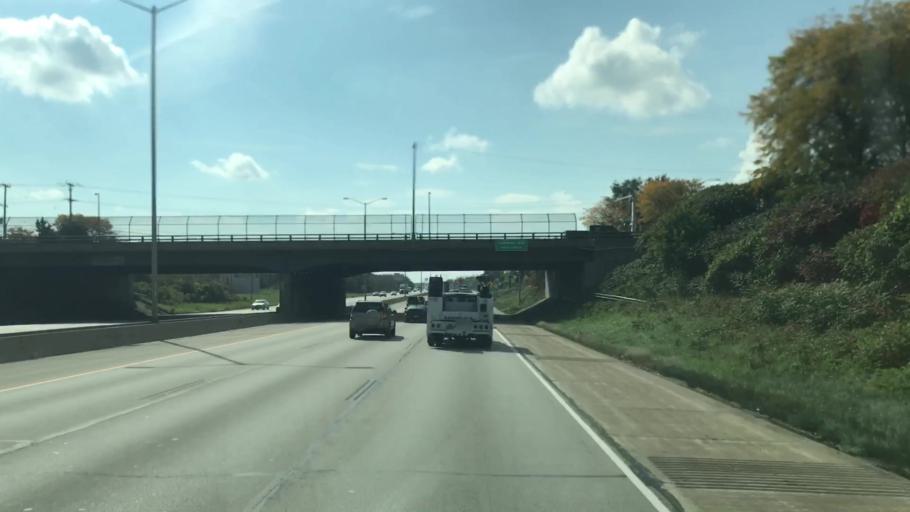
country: US
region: Wisconsin
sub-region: Waukesha County
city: Butler
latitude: 43.1055
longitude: -88.0582
